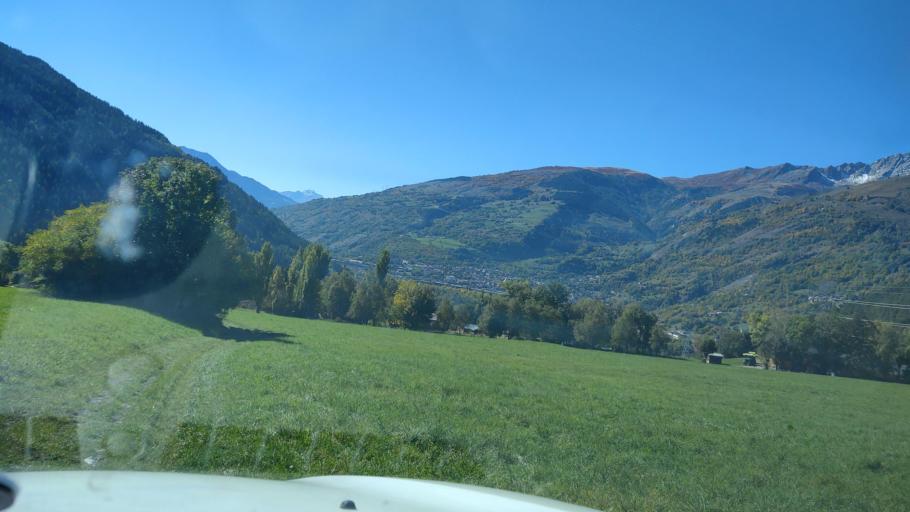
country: FR
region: Rhone-Alpes
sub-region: Departement de la Savoie
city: Seez
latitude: 45.6266
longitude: 6.8075
